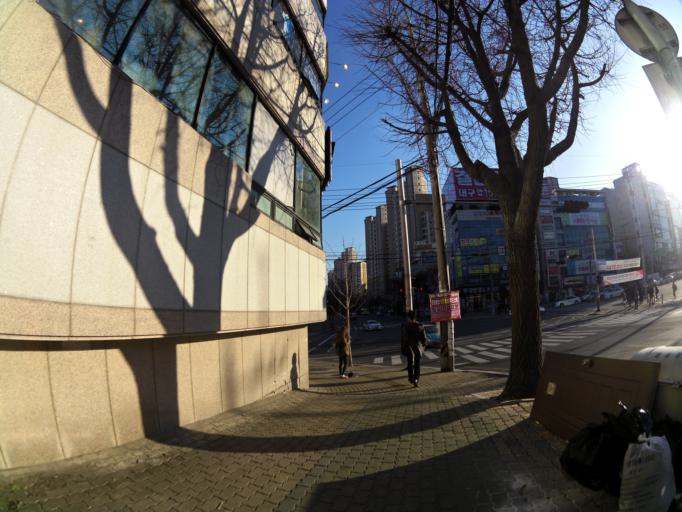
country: KR
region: Daegu
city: Daegu
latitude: 35.8727
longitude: 128.6350
